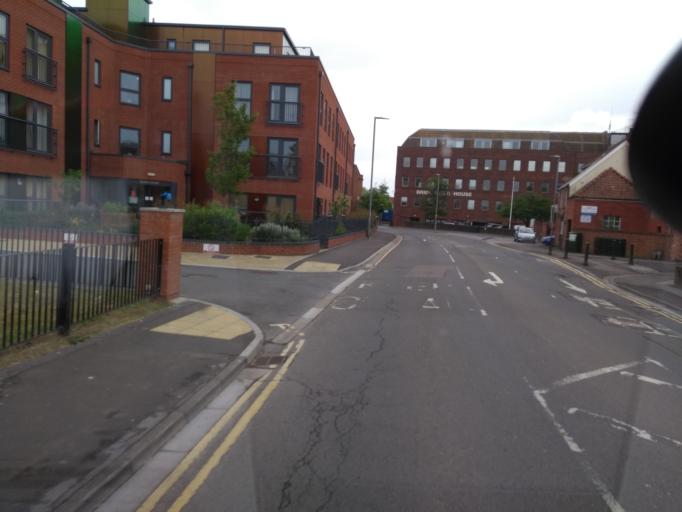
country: GB
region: England
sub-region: Somerset
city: Bridgwater
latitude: 51.1299
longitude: -3.0051
